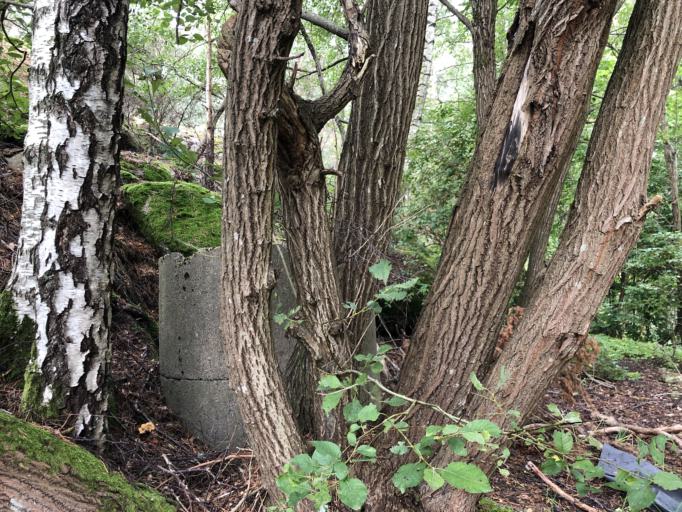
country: SE
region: Vaestra Goetaland
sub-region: Goteborg
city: Majorna
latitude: 57.7449
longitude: 11.9059
